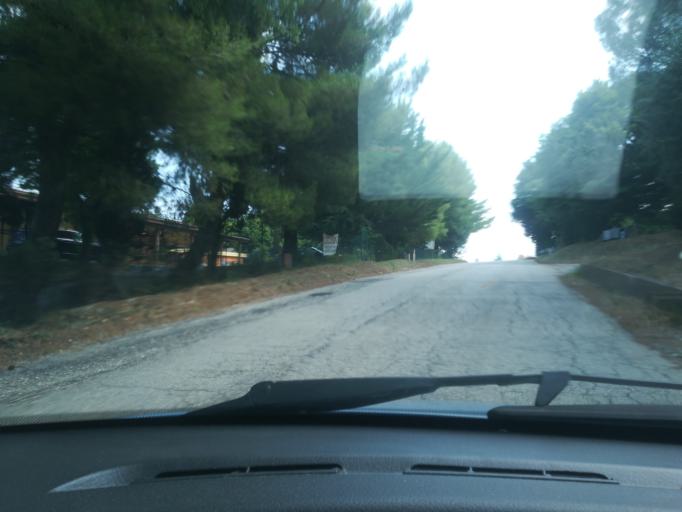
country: IT
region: The Marches
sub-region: Provincia di Macerata
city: Sforzacosta
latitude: 43.2651
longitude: 13.4386
